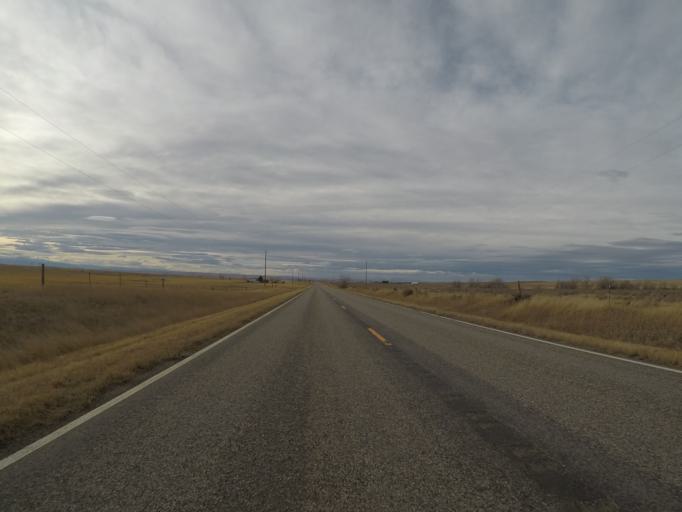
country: US
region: Montana
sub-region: Yellowstone County
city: Laurel
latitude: 45.8564
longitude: -108.8094
